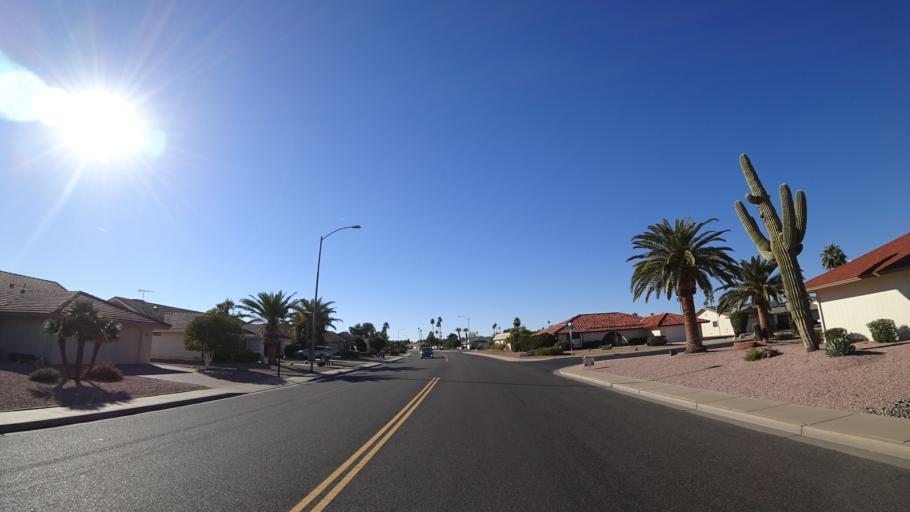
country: US
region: Arizona
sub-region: Maricopa County
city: Sun City West
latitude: 33.6721
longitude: -112.3468
